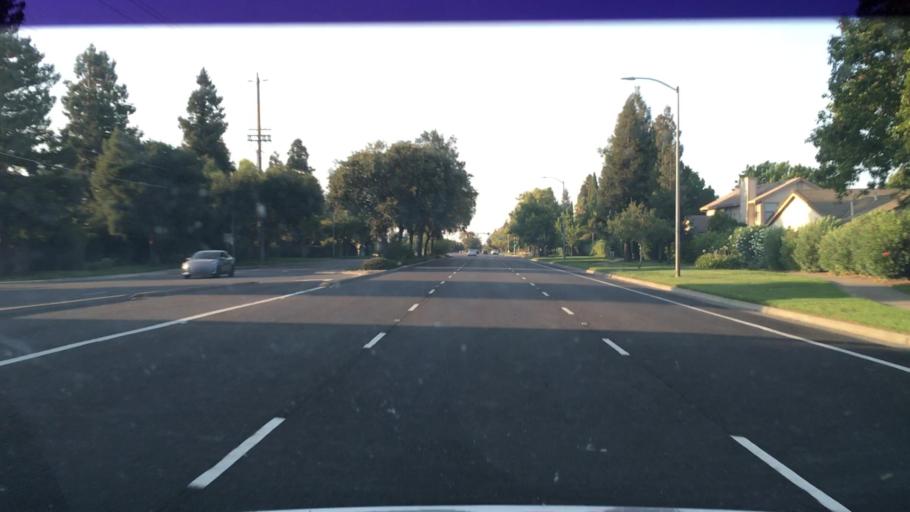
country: US
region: California
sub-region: Sacramento County
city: Laguna
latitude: 38.4319
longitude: -121.4466
